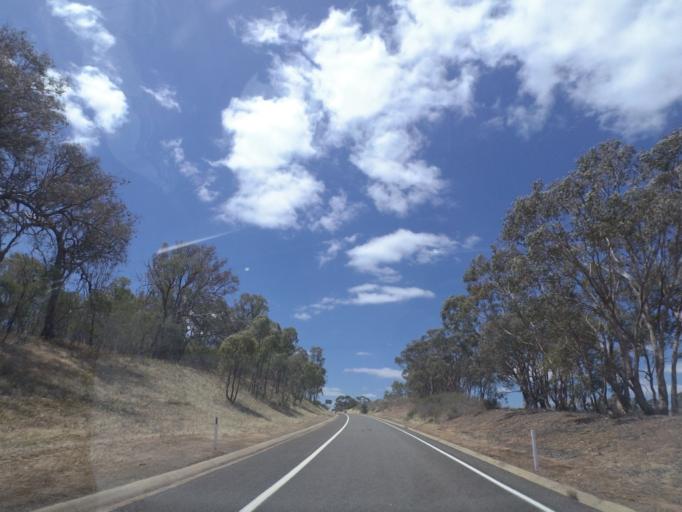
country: AU
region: Victoria
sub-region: Wangaratta
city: Wangaratta
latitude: -36.4682
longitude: 146.2075
